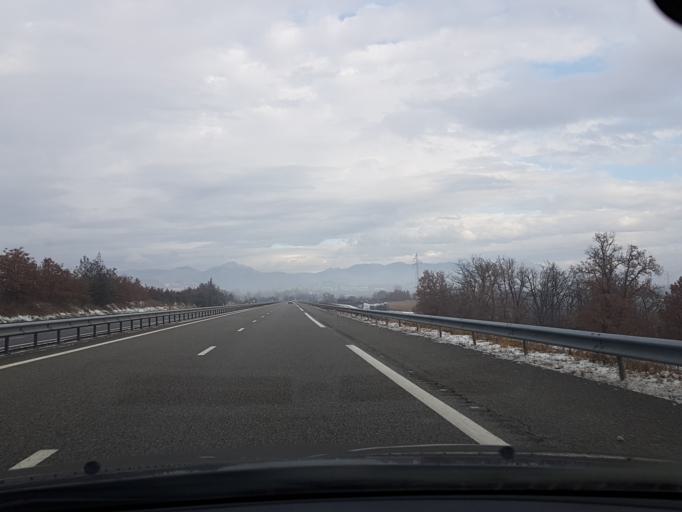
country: FR
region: Provence-Alpes-Cote d'Azur
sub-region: Departement des Hautes-Alpes
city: Laragne-Monteglin
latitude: 44.2752
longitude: 5.9002
